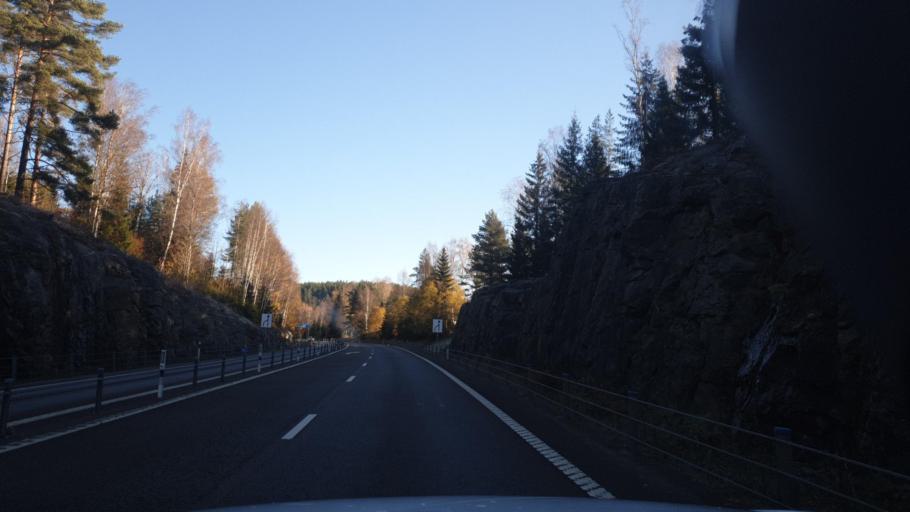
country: SE
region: Vaermland
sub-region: Arvika Kommun
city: Arvika
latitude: 59.6455
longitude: 12.7452
